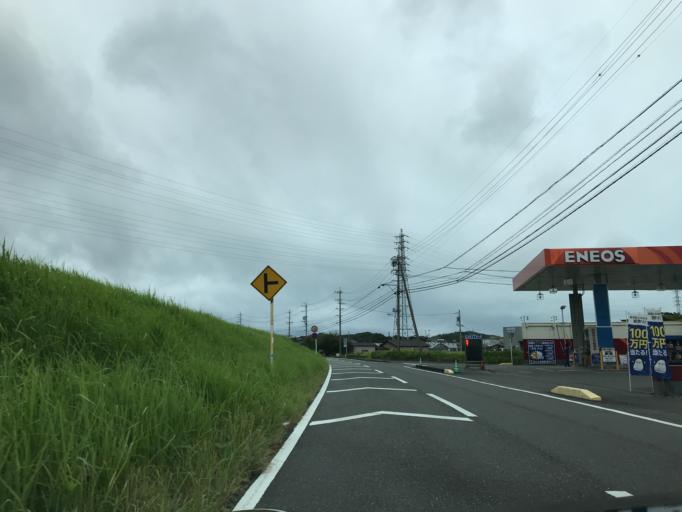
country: JP
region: Shizuoka
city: Sagara
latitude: 34.6569
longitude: 138.1323
